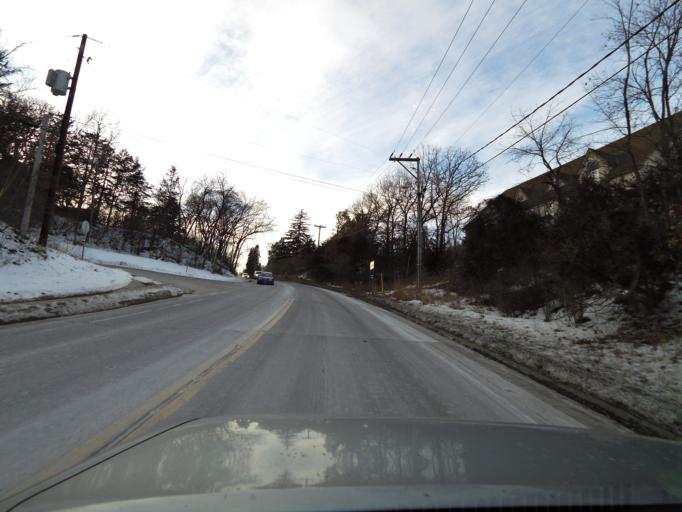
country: US
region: Minnesota
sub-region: Washington County
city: Afton
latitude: 44.9031
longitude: -92.7856
